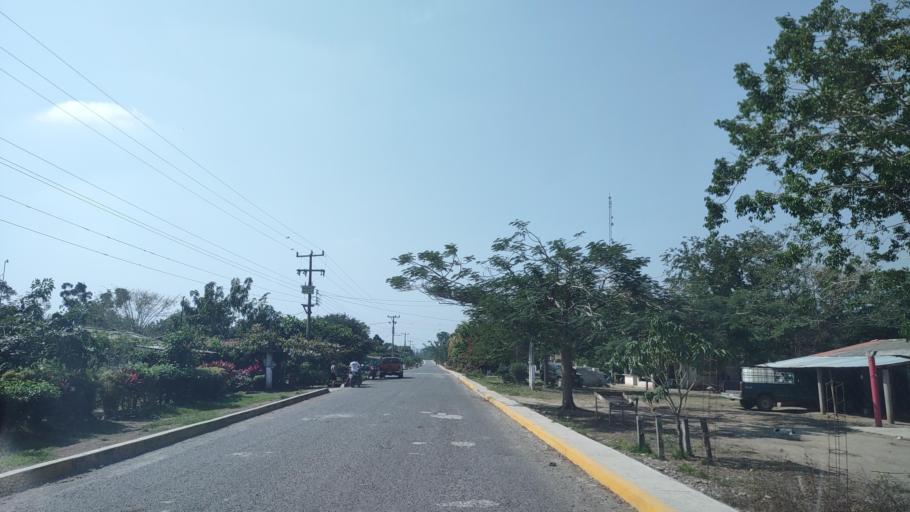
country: MX
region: Puebla
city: Espinal
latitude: 20.2628
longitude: -97.3103
